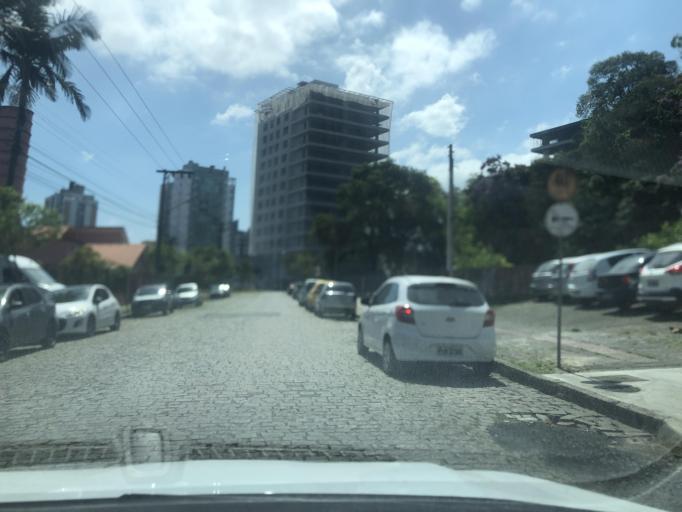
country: BR
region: Santa Catarina
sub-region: Joinville
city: Joinville
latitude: -26.3106
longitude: -48.8492
